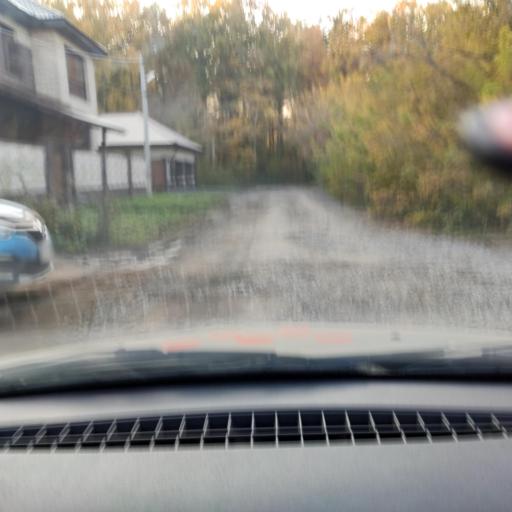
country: RU
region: Bashkortostan
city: Ufa
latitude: 54.7911
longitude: 56.1584
